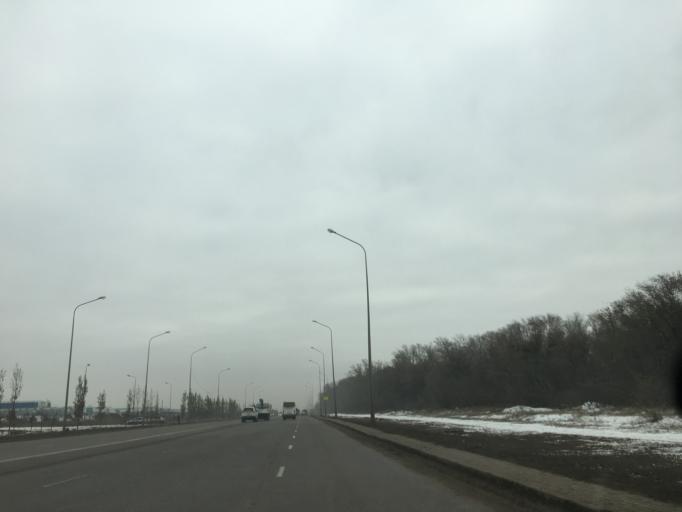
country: KZ
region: Astana Qalasy
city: Astana
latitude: 51.1689
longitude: 71.4957
